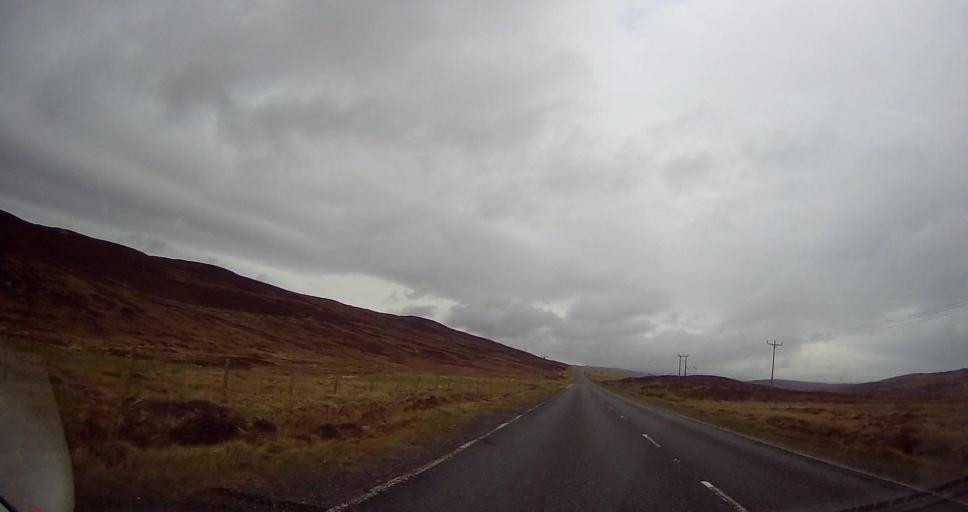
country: GB
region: Scotland
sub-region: Shetland Islands
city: Lerwick
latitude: 60.2090
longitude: -1.2334
